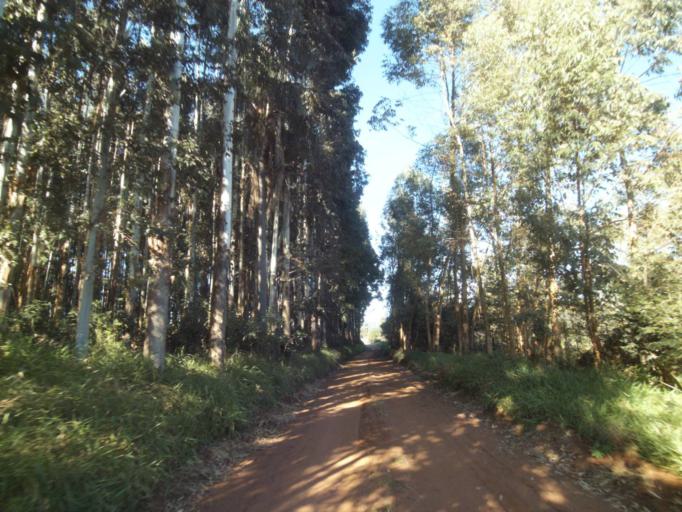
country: BR
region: Parana
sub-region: Tibagi
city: Tibagi
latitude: -24.5439
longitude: -50.3670
